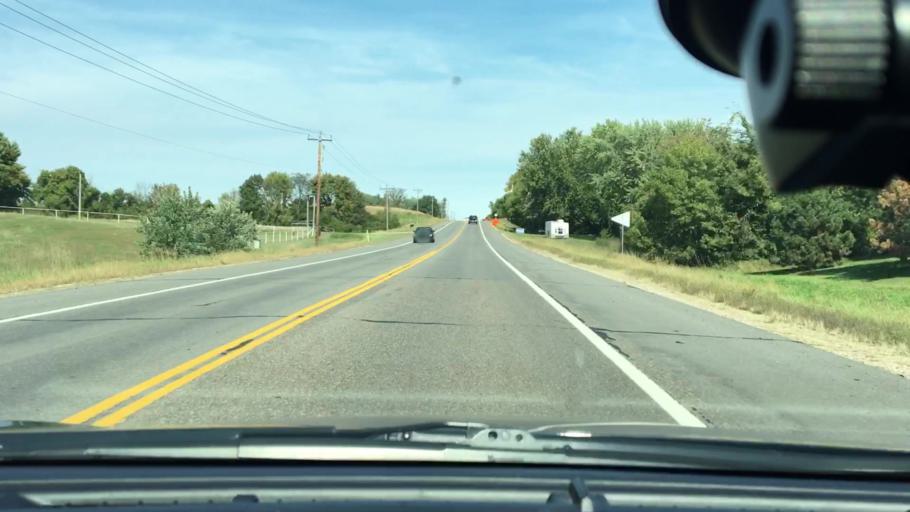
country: US
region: Minnesota
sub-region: Wright County
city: Hanover
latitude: 45.1794
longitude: -93.6655
